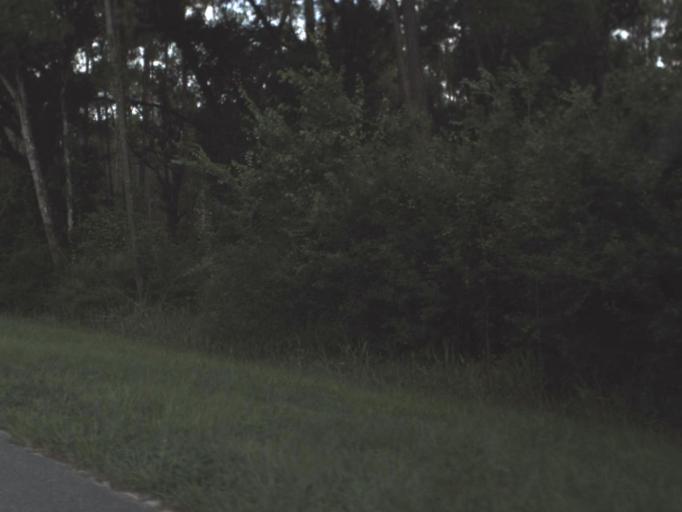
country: US
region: Florida
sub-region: Hernando County
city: Ridge Manor
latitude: 28.5077
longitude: -82.1295
